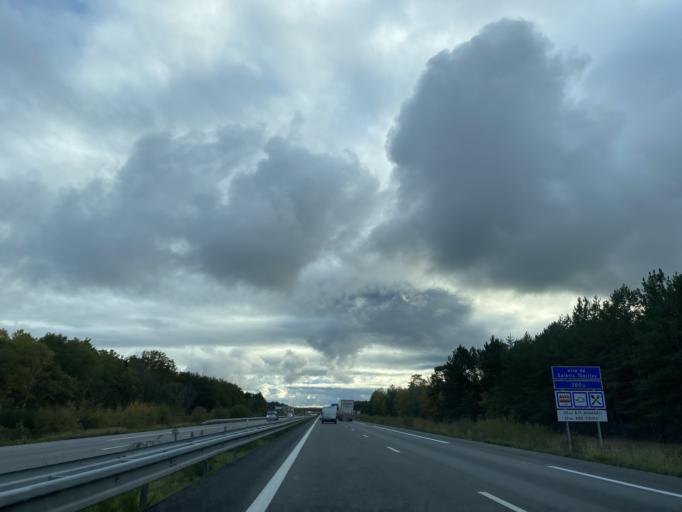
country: FR
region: Centre
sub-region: Departement du Loir-et-Cher
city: Theillay
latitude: 47.3553
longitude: 2.0510
